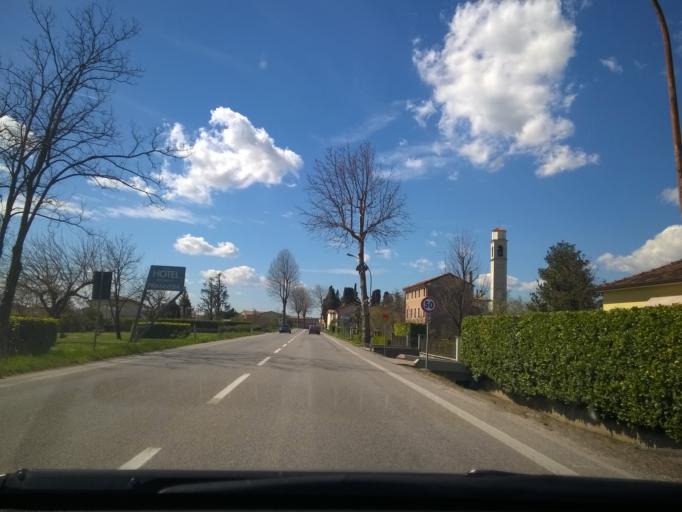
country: IT
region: Veneto
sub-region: Provincia di Treviso
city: Godega
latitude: 45.9317
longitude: 12.4034
